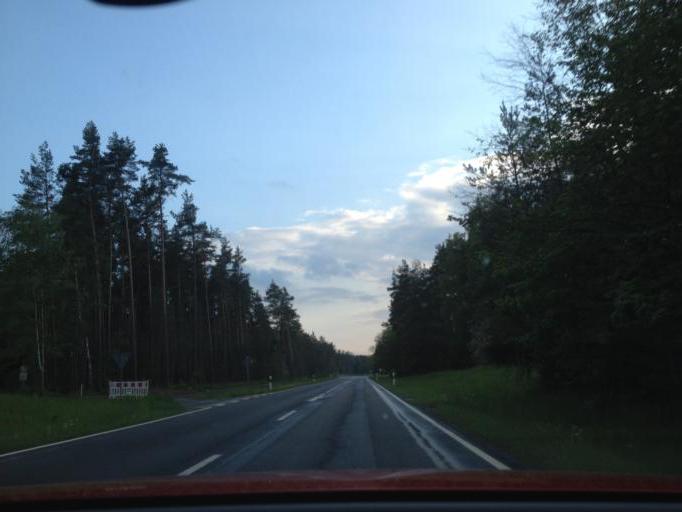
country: DE
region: Bavaria
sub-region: Upper Palatinate
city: Weiherhammer
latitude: 49.6149
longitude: 12.0812
